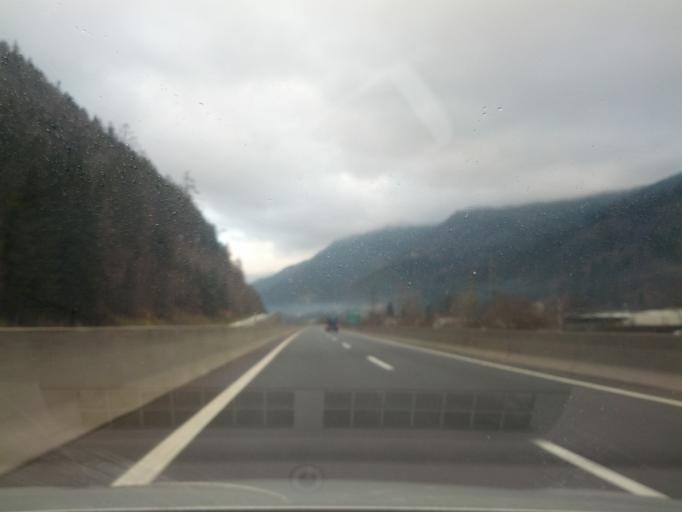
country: SI
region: Jesenice
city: Hrusica
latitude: 46.4361
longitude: 14.0400
